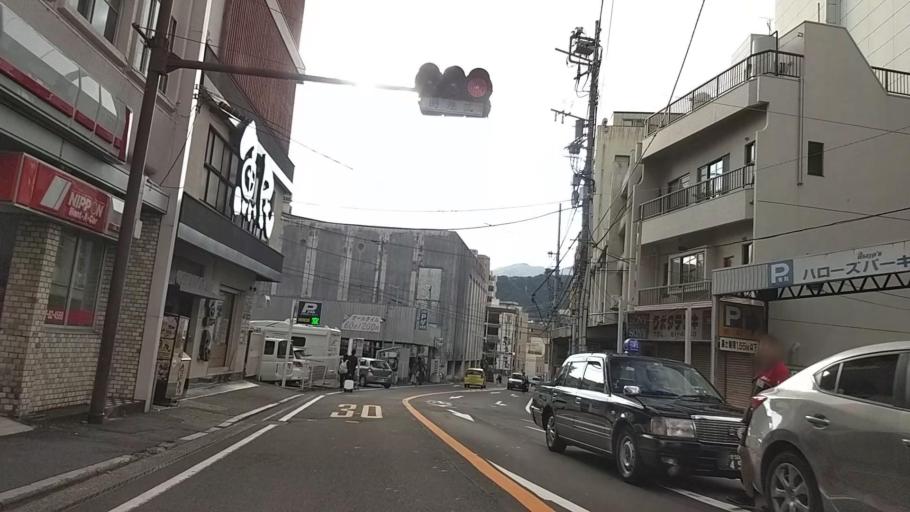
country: JP
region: Shizuoka
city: Atami
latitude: 35.1027
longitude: 139.0787
